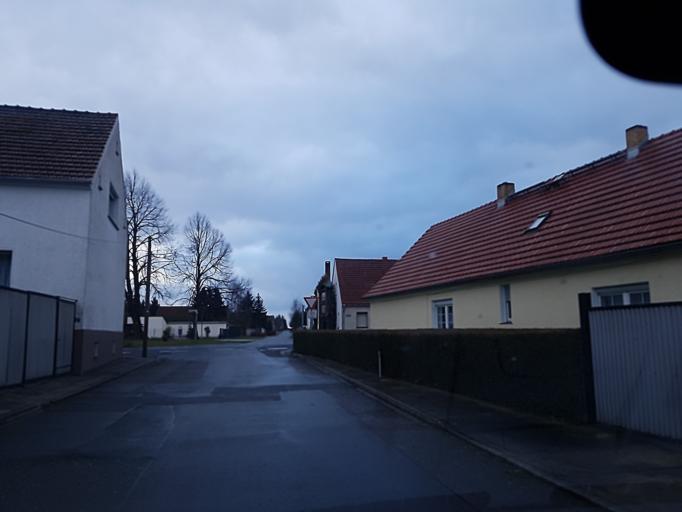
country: DE
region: Brandenburg
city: Plessa
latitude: 51.5347
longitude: 13.6290
